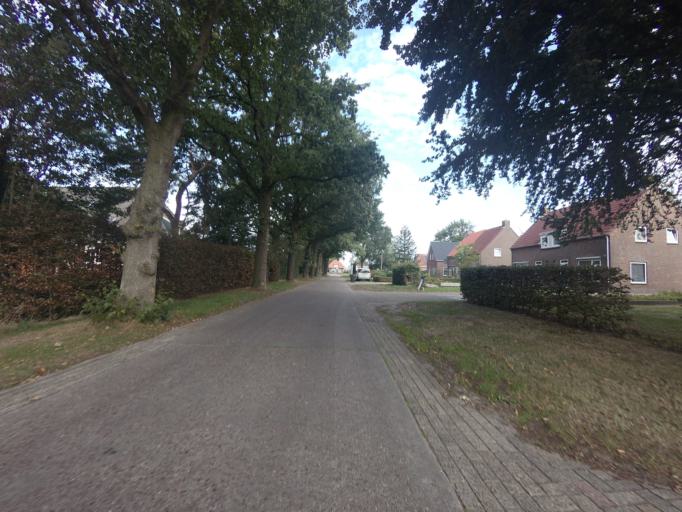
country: NL
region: Friesland
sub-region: Gemeente Heerenveen
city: Jubbega
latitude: 52.9842
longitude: 6.1439
